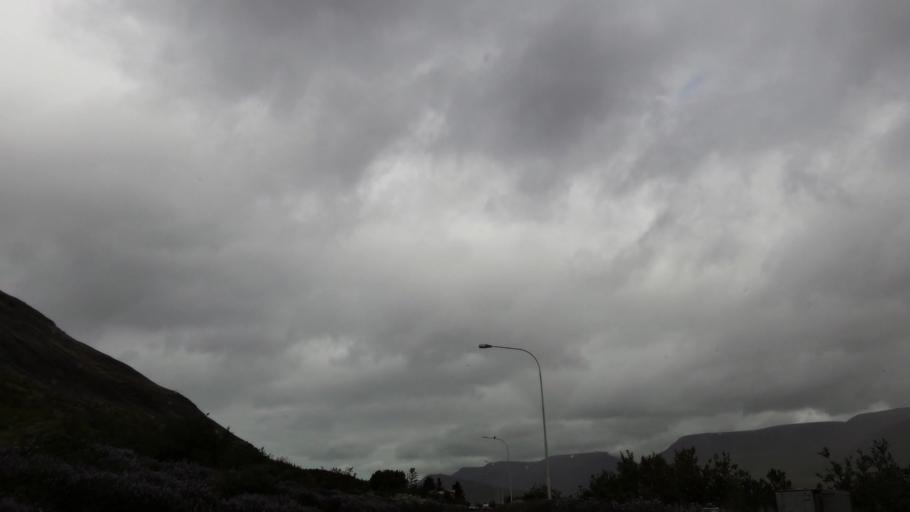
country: IS
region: Westfjords
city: Isafjoerdur
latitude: 65.8739
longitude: -23.4890
